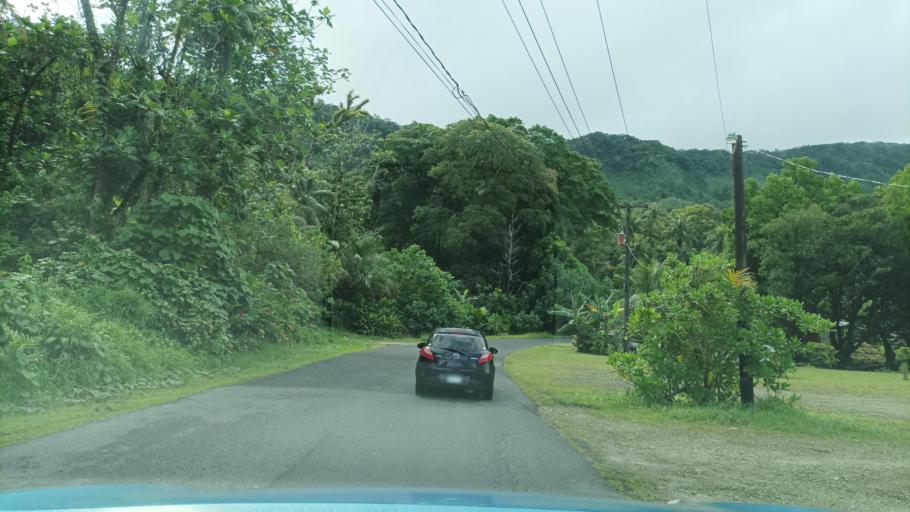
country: FM
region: Pohnpei
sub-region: Kolonia Municipality
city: Kolonia
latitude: 6.9592
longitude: 158.2489
